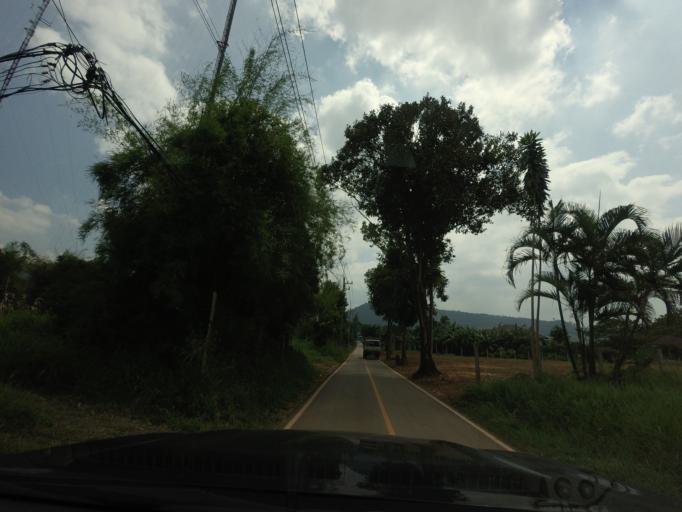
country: TH
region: Loei
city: Phu Ruea
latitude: 17.4517
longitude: 101.3525
